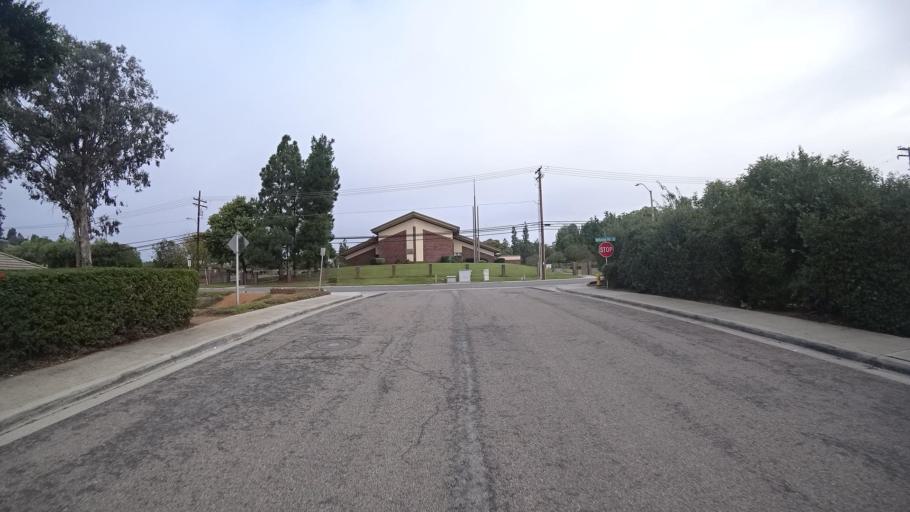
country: US
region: California
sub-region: San Diego County
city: Rancho San Diego
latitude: 32.7618
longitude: -116.9230
